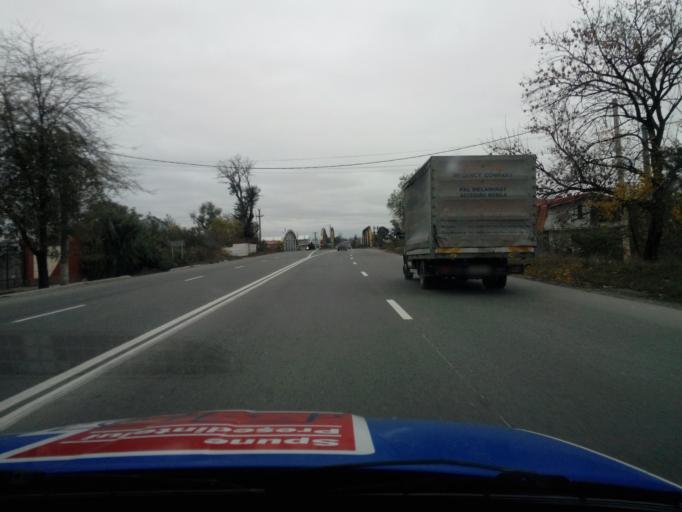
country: RO
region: Ilfov
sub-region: Comuna Jilava
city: Jilava
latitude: 44.3223
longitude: 26.0711
